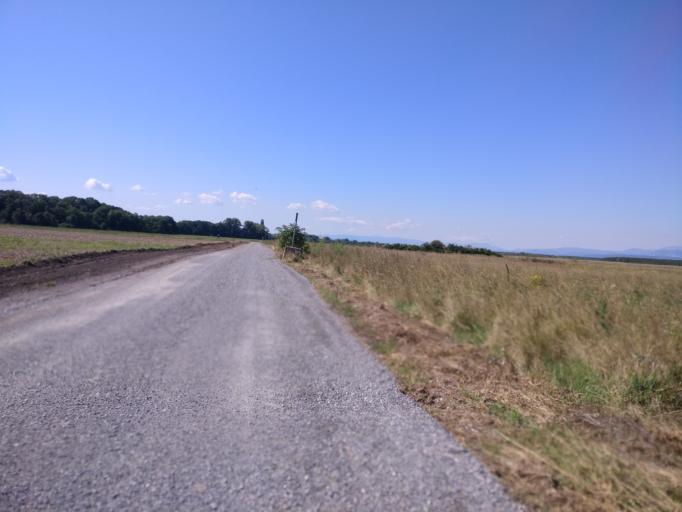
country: AT
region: Lower Austria
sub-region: Politischer Bezirk Baden
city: Pottendorf
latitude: 47.9193
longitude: 16.3602
